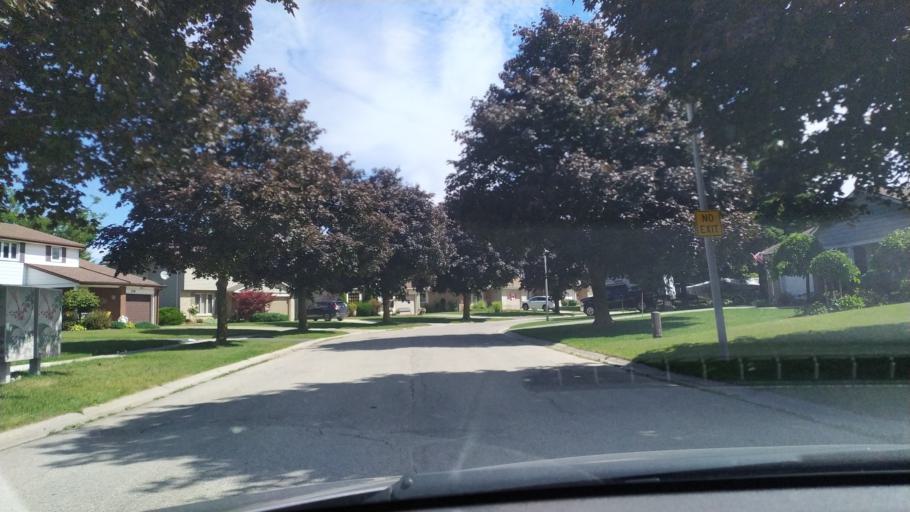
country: CA
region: Ontario
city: Stratford
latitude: 43.3746
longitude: -80.9450
